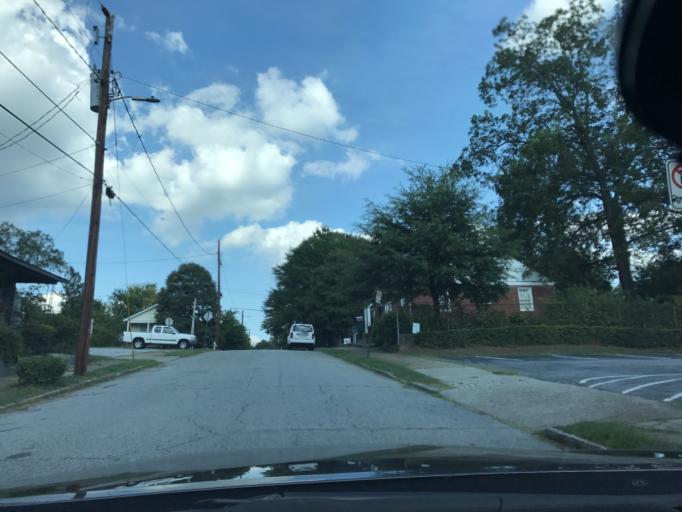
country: US
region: Georgia
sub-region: Fulton County
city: Atlanta
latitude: 33.7281
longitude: -84.4007
